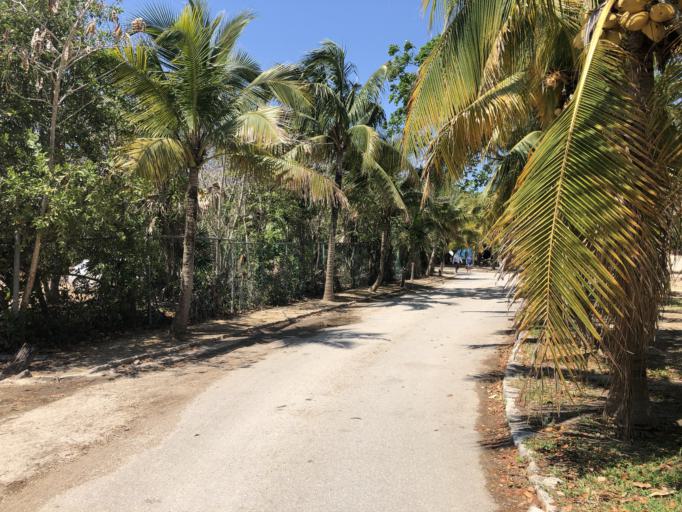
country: MX
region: Quintana Roo
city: Tulum
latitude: 20.2144
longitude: -87.4310
